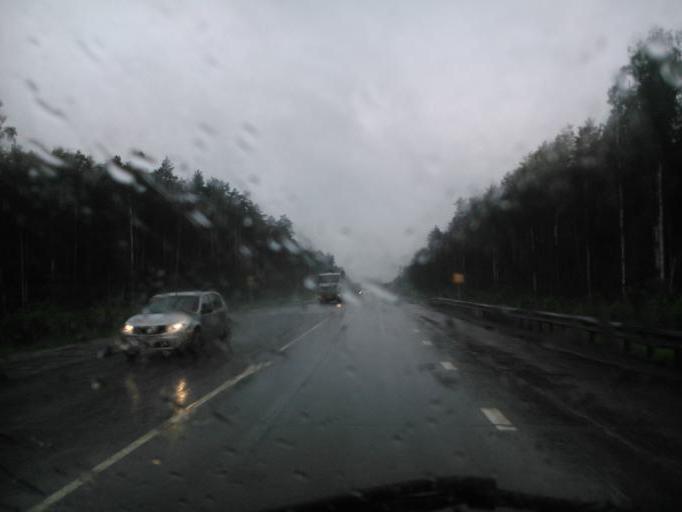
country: RU
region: Sverdlovsk
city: Shuvakish
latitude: 56.9336
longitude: 60.5005
